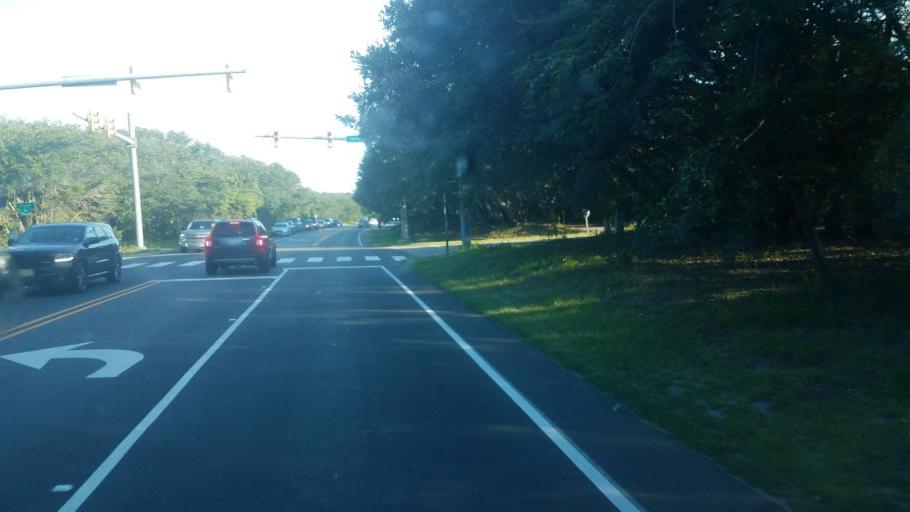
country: US
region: North Carolina
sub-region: Dare County
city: Southern Shores
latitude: 36.1440
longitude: -75.7396
